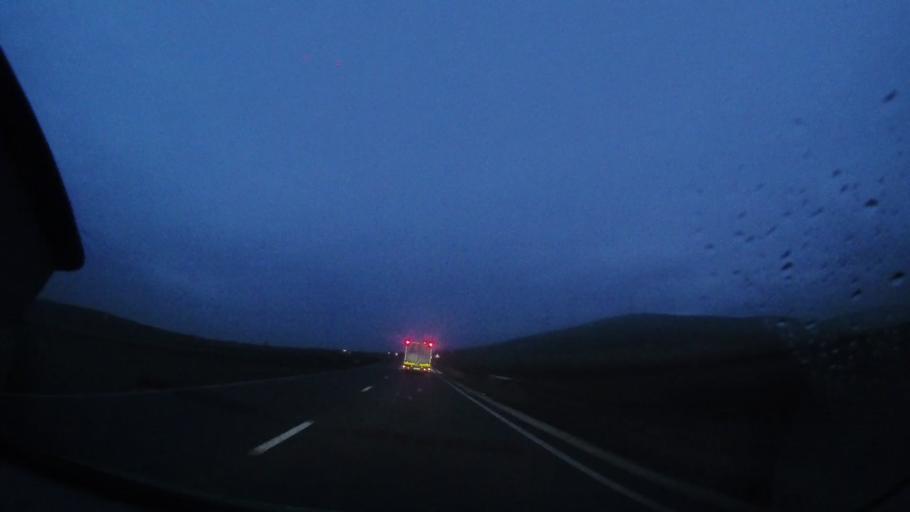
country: RO
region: Harghita
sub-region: Comuna Subcetate
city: Subcetate
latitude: 46.8429
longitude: 25.4733
